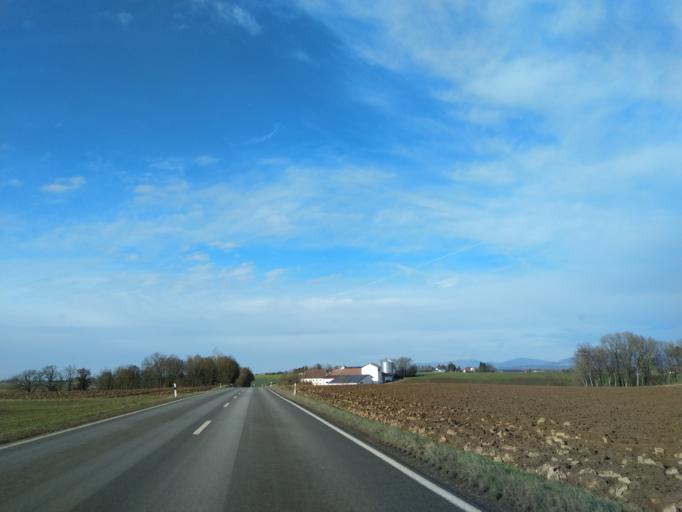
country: DE
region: Bavaria
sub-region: Lower Bavaria
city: Kunzing
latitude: 48.6610
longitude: 13.0439
